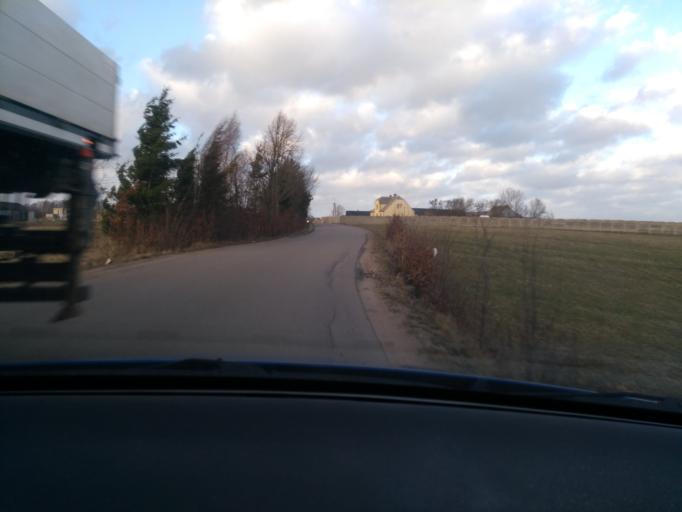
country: PL
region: Pomeranian Voivodeship
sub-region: Powiat kartuski
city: Kartuzy
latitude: 54.3767
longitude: 18.2153
